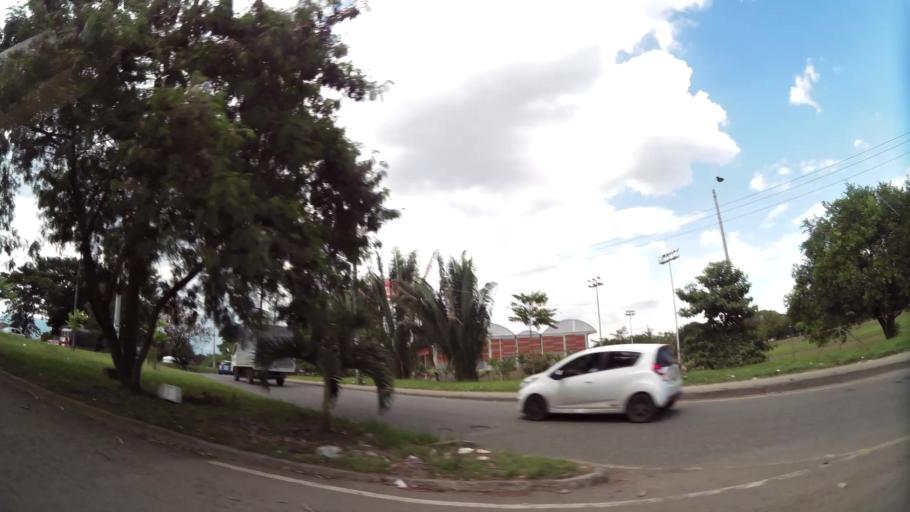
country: CO
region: Valle del Cauca
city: Cali
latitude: 3.4042
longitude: -76.5216
